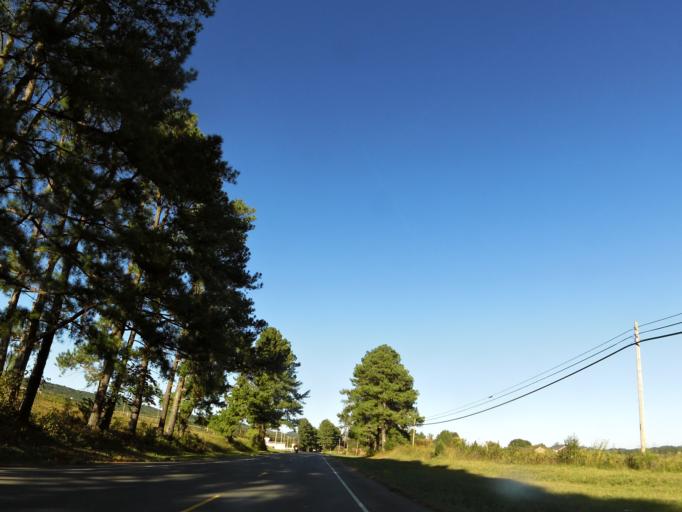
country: US
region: Tennessee
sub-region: Grainger County
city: Rutledge
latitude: 36.3133
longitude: -83.4084
